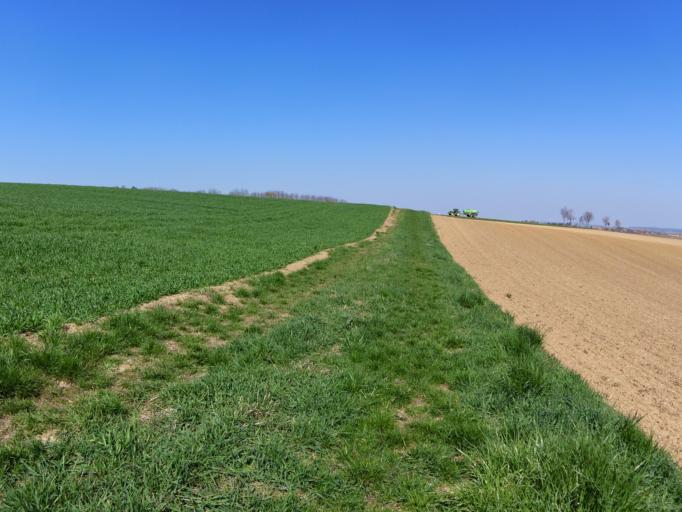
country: DE
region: Bavaria
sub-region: Regierungsbezirk Unterfranken
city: Biebelried
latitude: 49.7824
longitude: 10.0734
